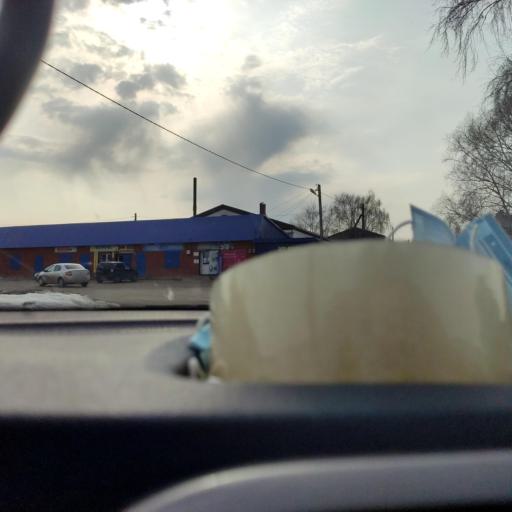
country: RU
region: Bashkortostan
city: Ulukulevo
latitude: 54.3729
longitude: 56.4488
